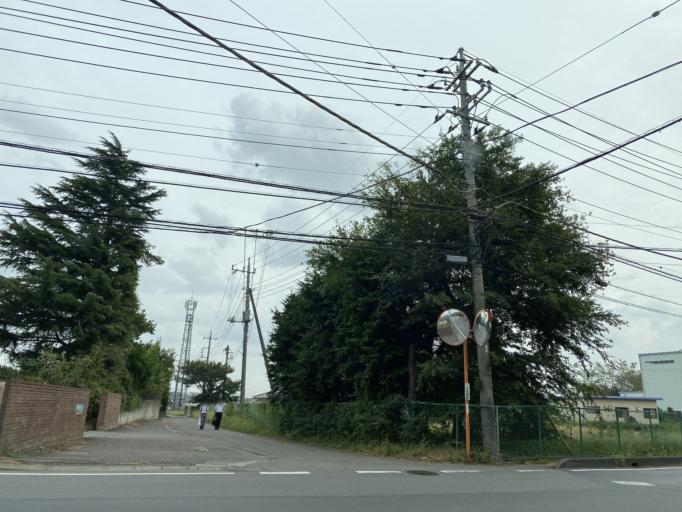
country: JP
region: Ibaraki
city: Mitsukaido
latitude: 36.0257
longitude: 140.0483
